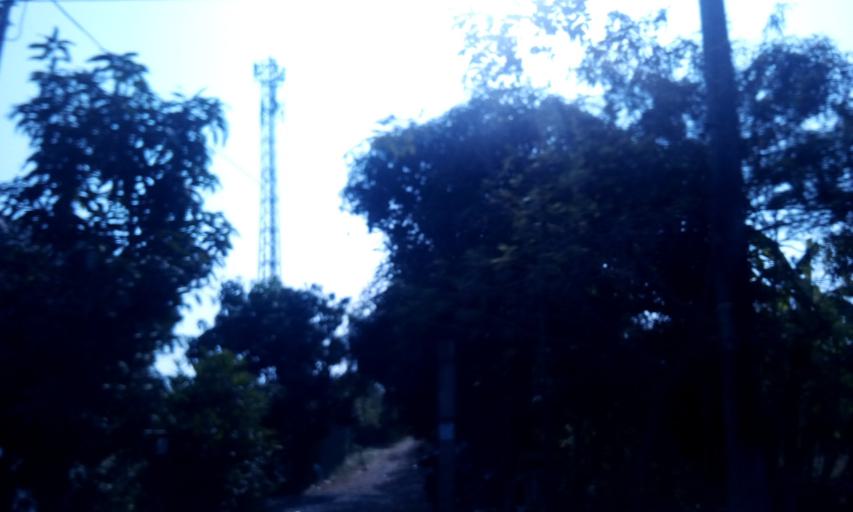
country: TH
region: Pathum Thani
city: Lam Luk Ka
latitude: 13.9588
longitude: 100.7058
